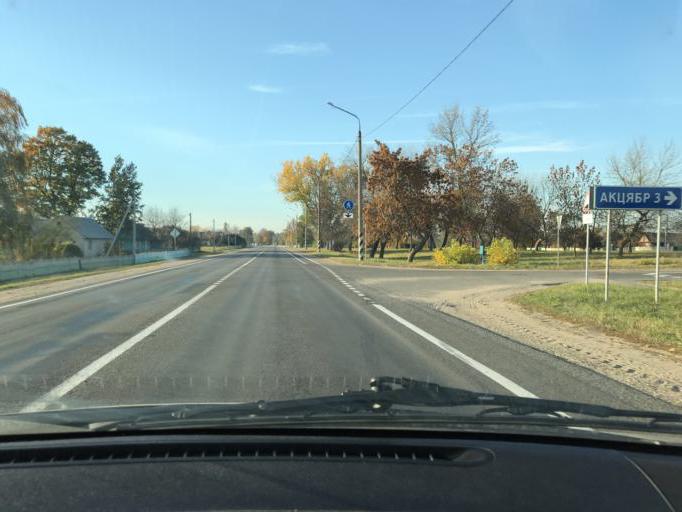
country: BY
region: Brest
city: Horad Kobryn
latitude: 52.2135
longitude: 24.5575
